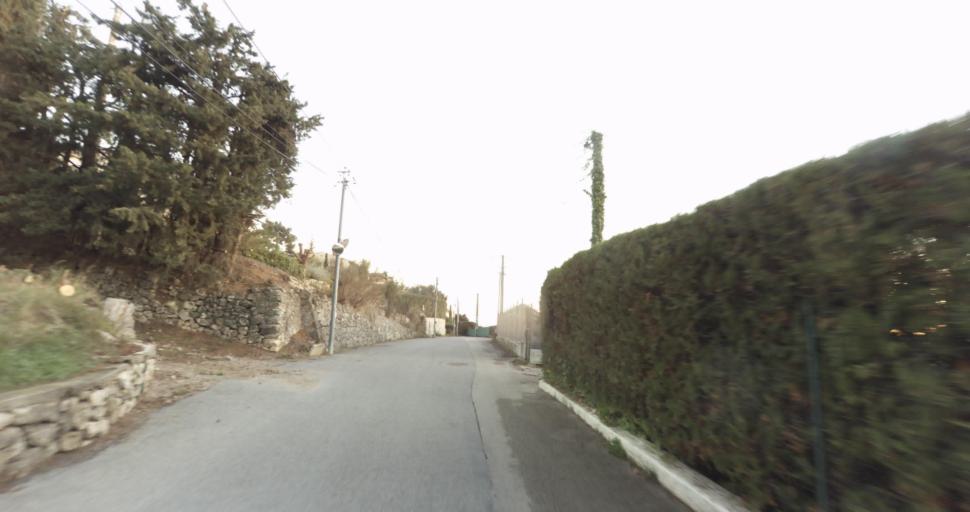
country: FR
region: Provence-Alpes-Cote d'Azur
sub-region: Departement des Alpes-Maritimes
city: La Gaude
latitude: 43.7242
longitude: 7.1336
